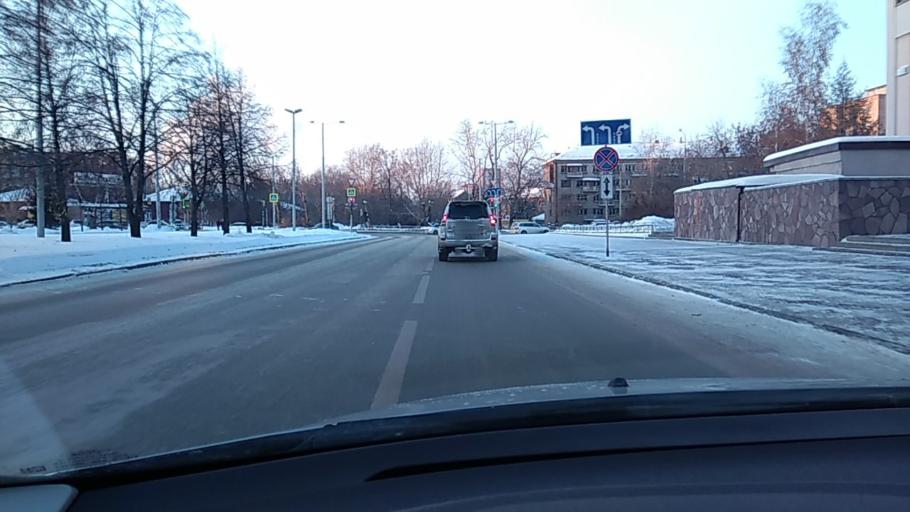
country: RU
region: Sverdlovsk
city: Yekaterinburg
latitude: 56.8453
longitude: 60.5881
